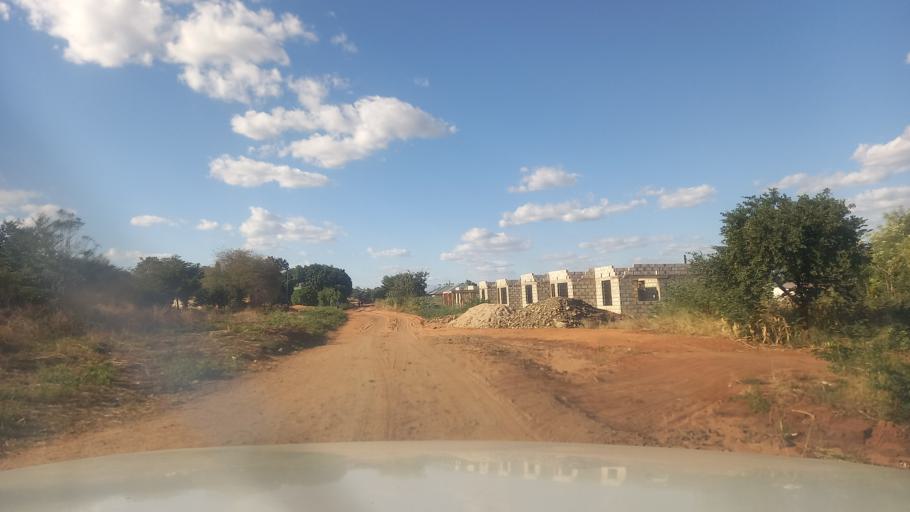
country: ZM
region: Southern
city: Livingstone
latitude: -17.8285
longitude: 25.8688
